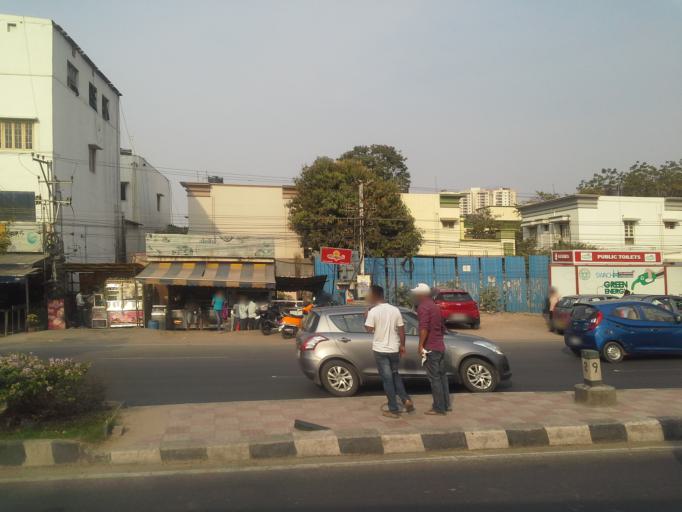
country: IN
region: Telangana
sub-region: Rangareddi
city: Kukatpalli
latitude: 17.4407
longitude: 78.3607
